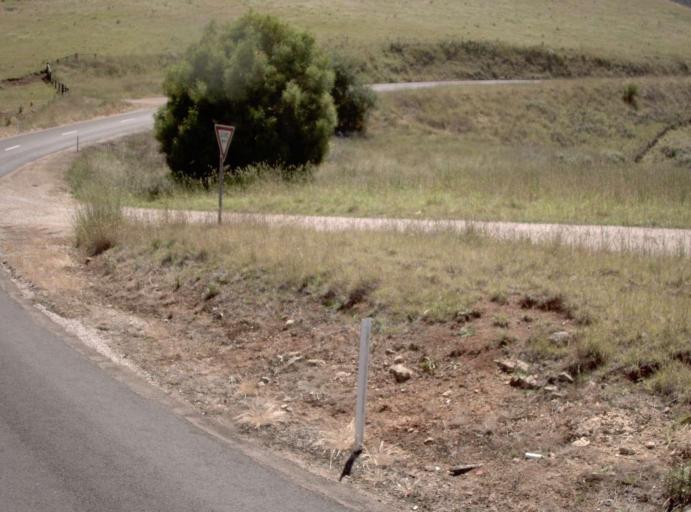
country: AU
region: Victoria
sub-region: East Gippsland
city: Lakes Entrance
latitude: -37.4125
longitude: 148.2053
